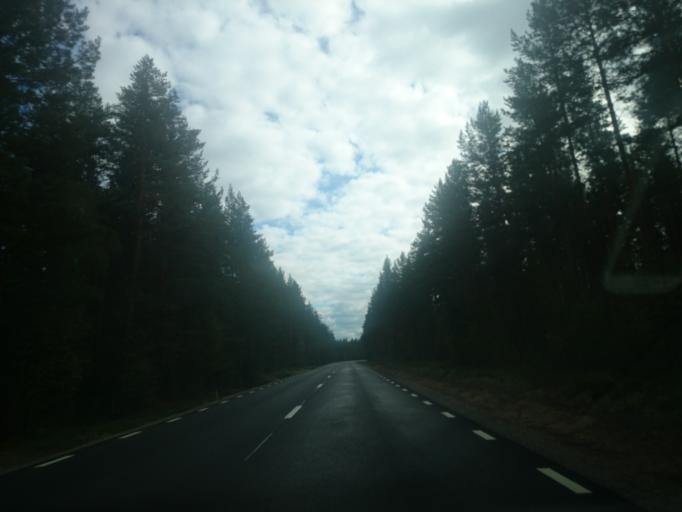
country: SE
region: Gaevleborg
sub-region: Ljusdals Kommun
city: Farila
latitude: 61.8539
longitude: 15.7483
